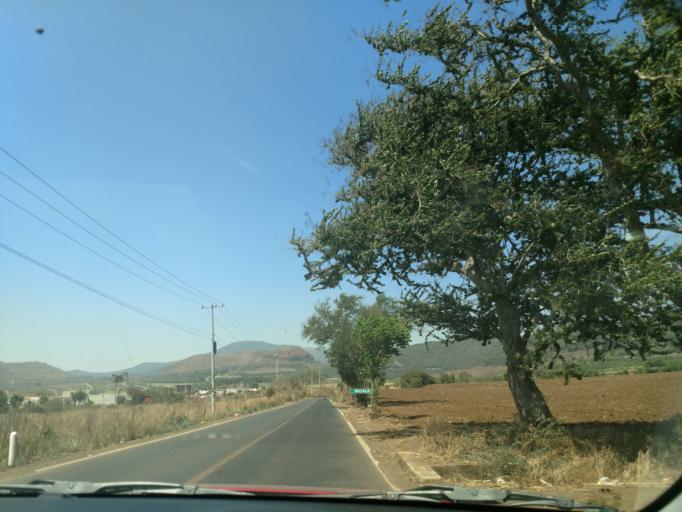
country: MX
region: Nayarit
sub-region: Tepic
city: La Corregidora
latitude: 21.4928
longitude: -104.7911
